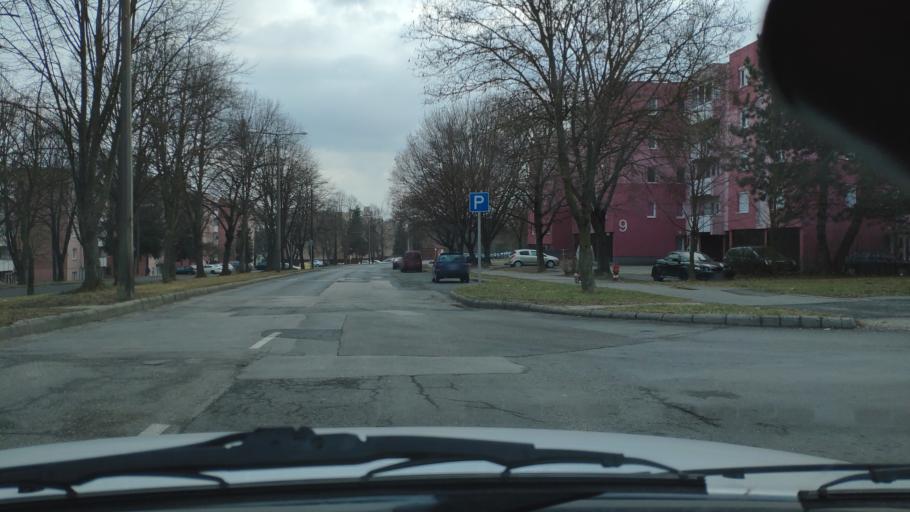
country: HU
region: Zala
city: Nagykanizsa
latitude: 46.4622
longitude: 17.0177
